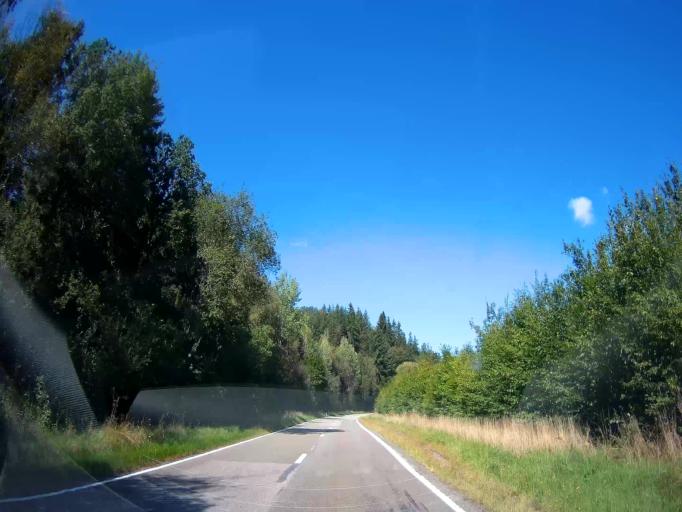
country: BE
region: Wallonia
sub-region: Province du Luxembourg
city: Bertogne
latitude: 50.1088
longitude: 5.6303
